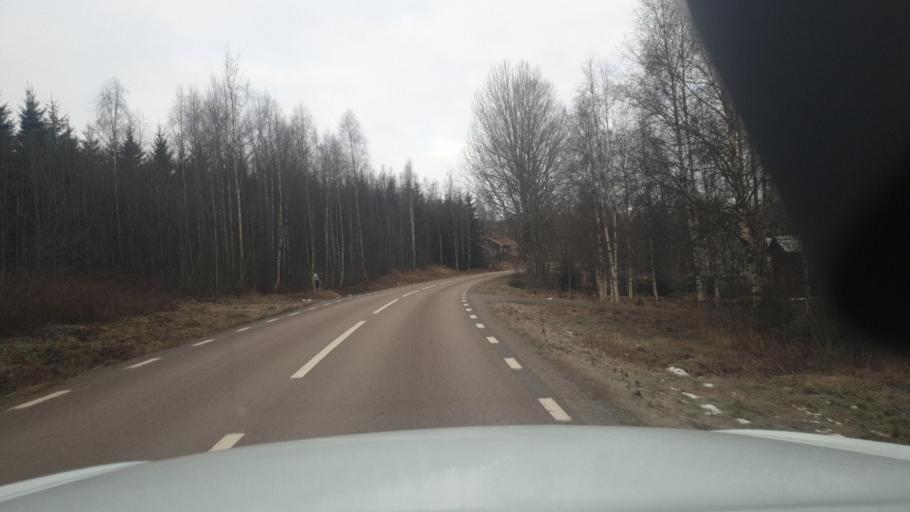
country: SE
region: Vaermland
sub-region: Torsby Kommun
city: Torsby
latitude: 59.9167
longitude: 12.8990
